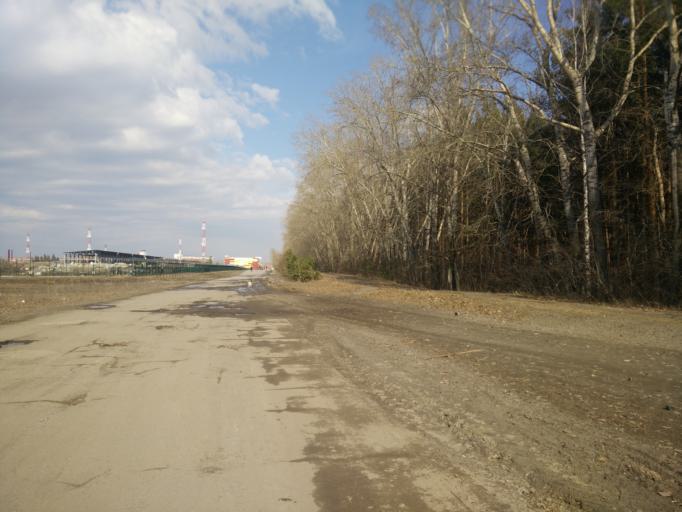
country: RU
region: Novosibirsk
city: Berdsk
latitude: 54.7608
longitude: 83.0706
